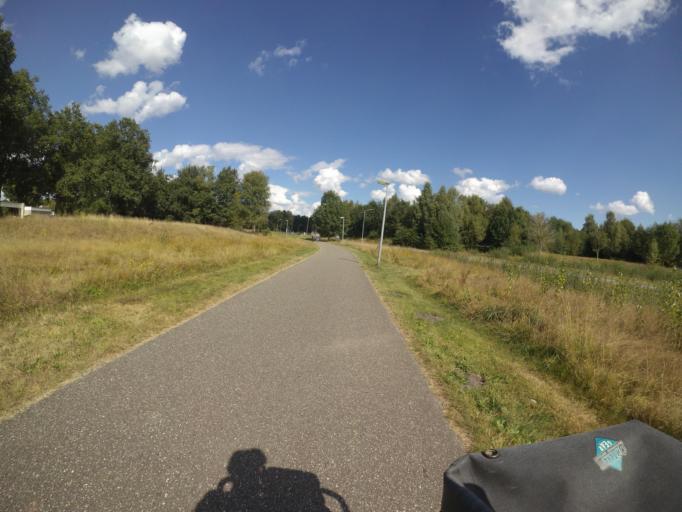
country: NL
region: Groningen
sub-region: Gemeente Leek
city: Leek
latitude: 53.1394
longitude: 6.4117
